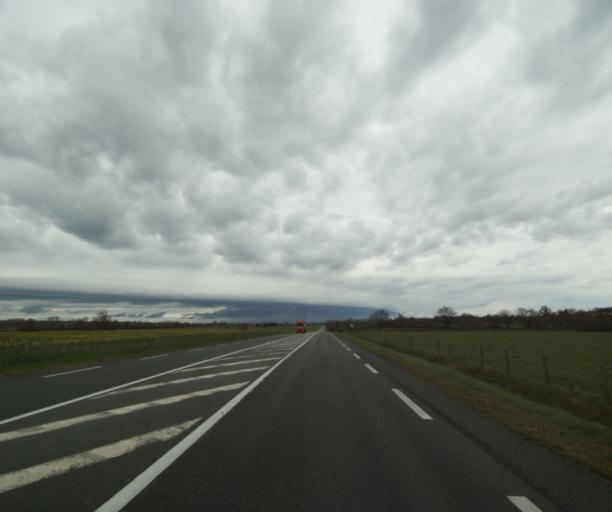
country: FR
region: Auvergne
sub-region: Departement de l'Allier
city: Bessay-sur-Allier
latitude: 46.4781
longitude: 3.3669
